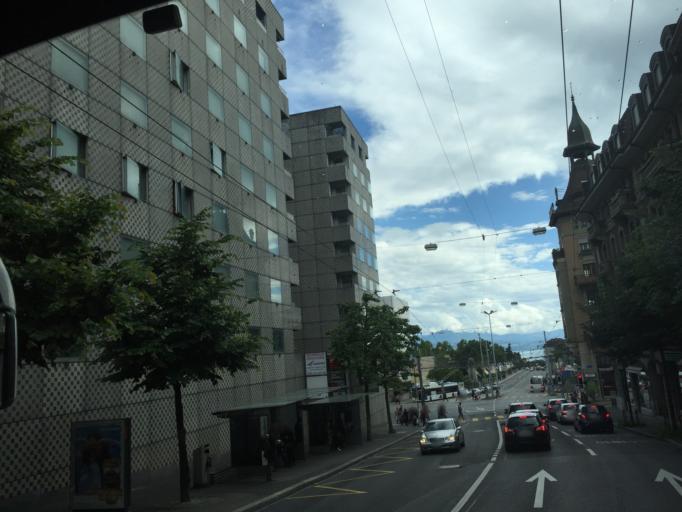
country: CH
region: Vaud
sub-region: Lausanne District
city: Lausanne
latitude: 46.5244
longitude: 6.6252
